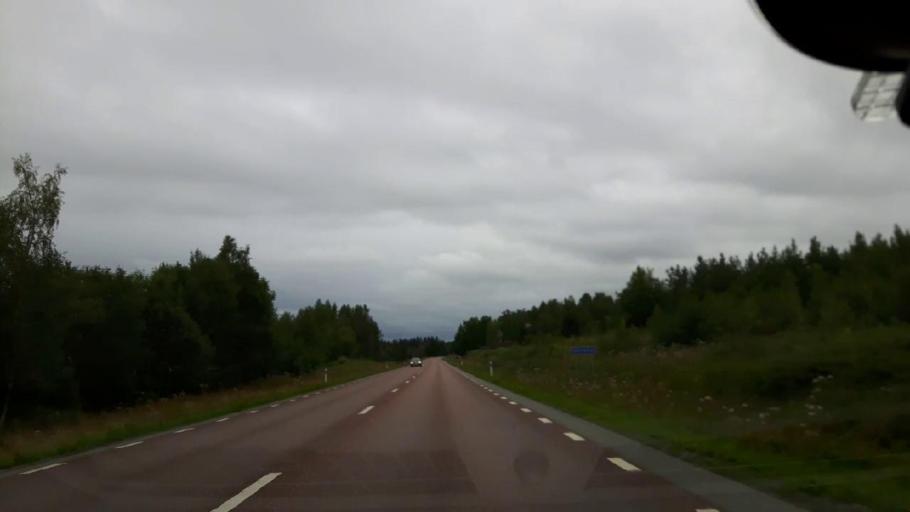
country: SE
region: Jaemtland
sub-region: Bergs Kommun
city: Hoverberg
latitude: 62.8965
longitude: 14.5238
